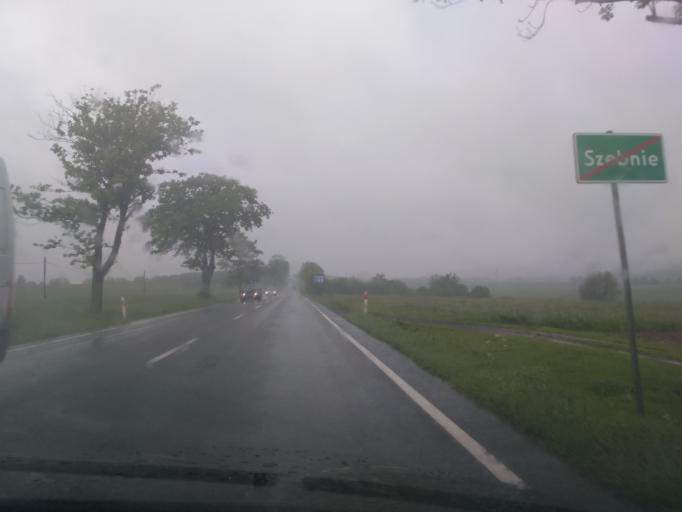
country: PL
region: Subcarpathian Voivodeship
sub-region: Powiat jasielski
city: Tarnowiec
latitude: 49.7623
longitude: 21.5856
